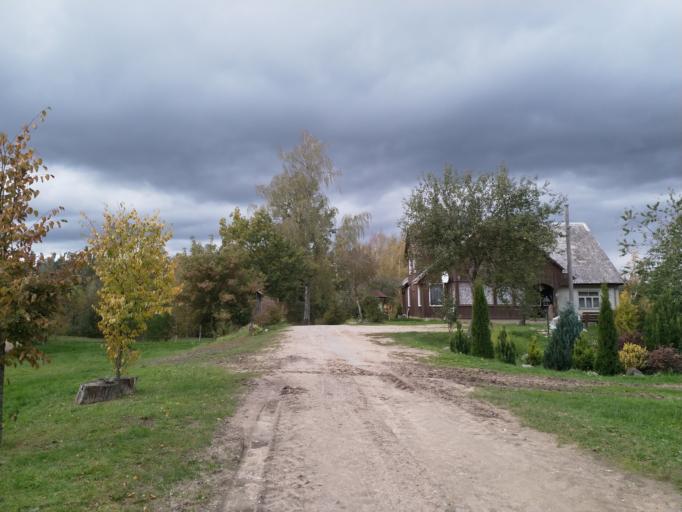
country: LV
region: Alsunga
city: Alsunga
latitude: 57.0413
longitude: 21.6936
